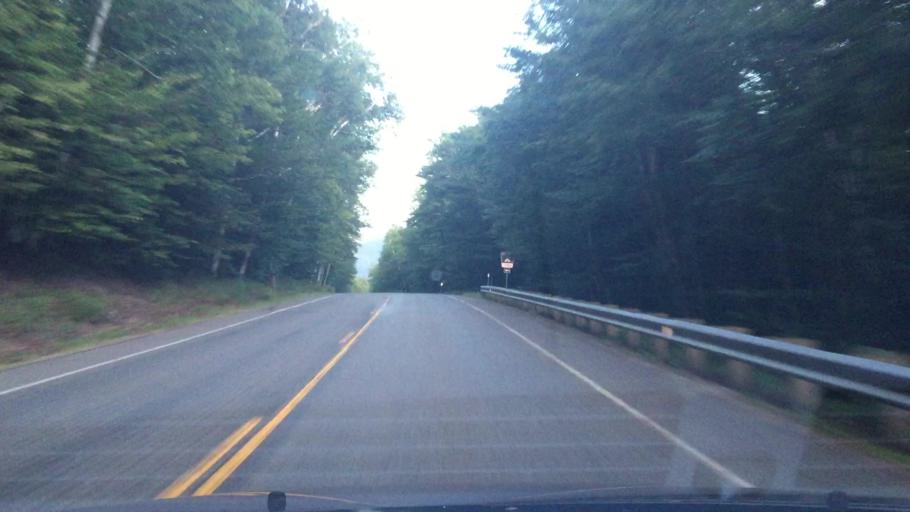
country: US
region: New Hampshire
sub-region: Grafton County
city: Woodstock
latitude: 44.0480
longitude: -71.5617
